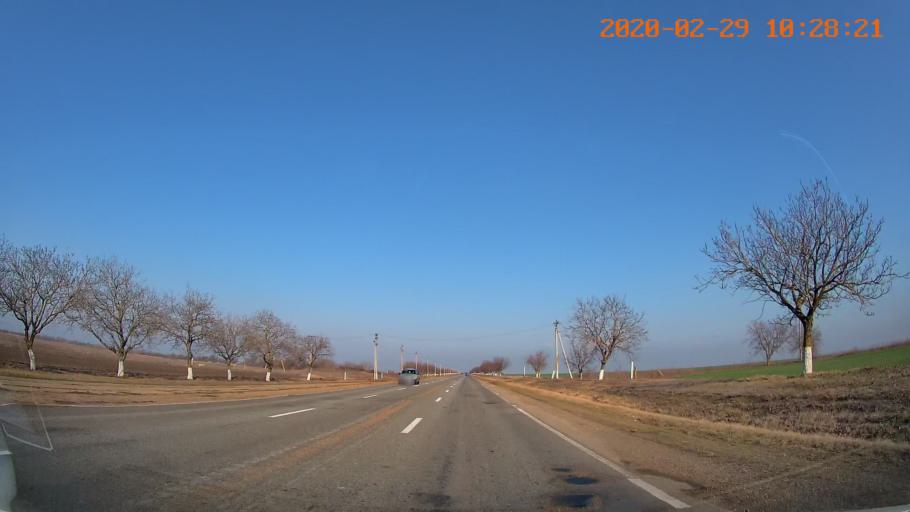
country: MD
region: Telenesti
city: Tiraspolul Nou
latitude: 46.9092
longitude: 29.5920
